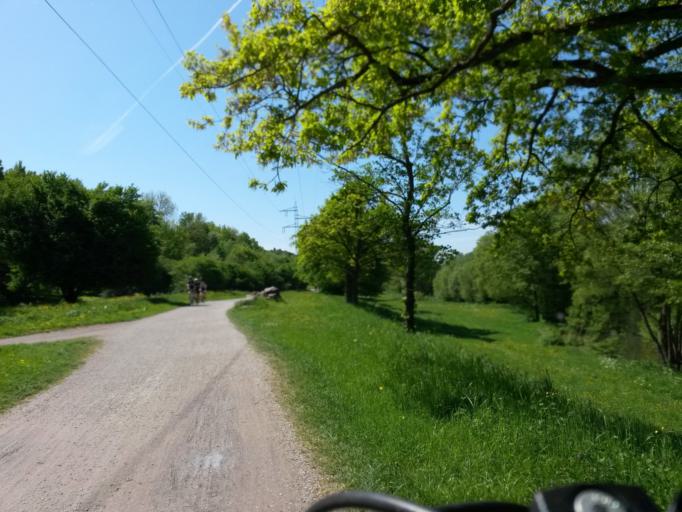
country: DE
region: Baden-Wuerttemberg
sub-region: Karlsruhe Region
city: Eutingen
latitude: 48.9005
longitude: 8.7365
